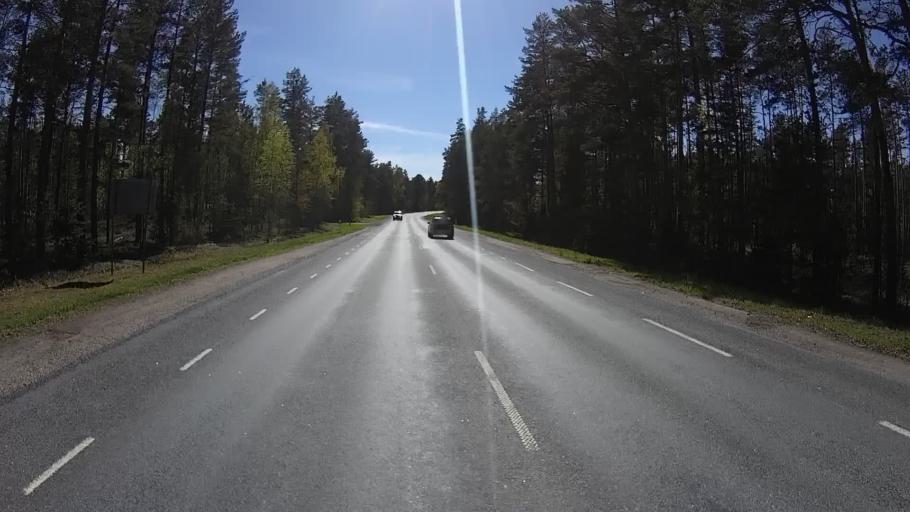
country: EE
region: Harju
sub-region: Loksa linn
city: Loksa
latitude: 59.5305
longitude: 25.7140
